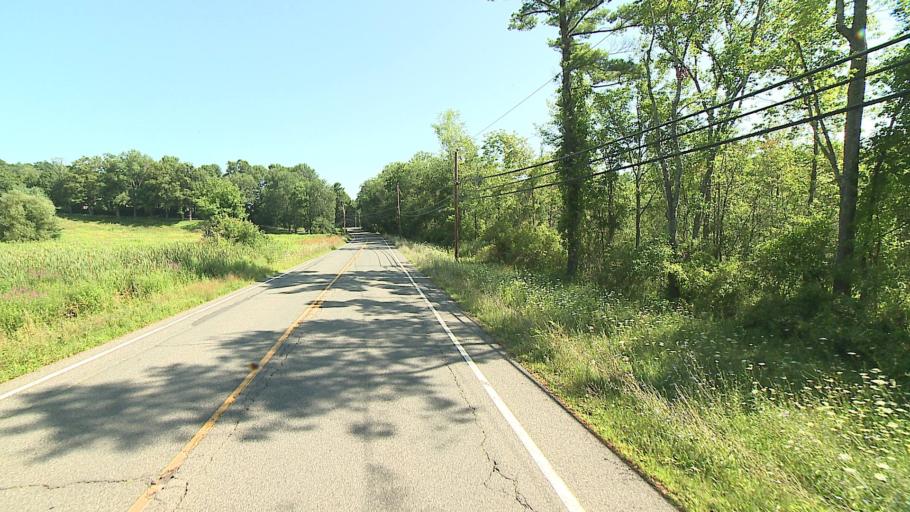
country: US
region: Connecticut
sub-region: Litchfield County
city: Canaan
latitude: 41.9973
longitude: -73.4255
